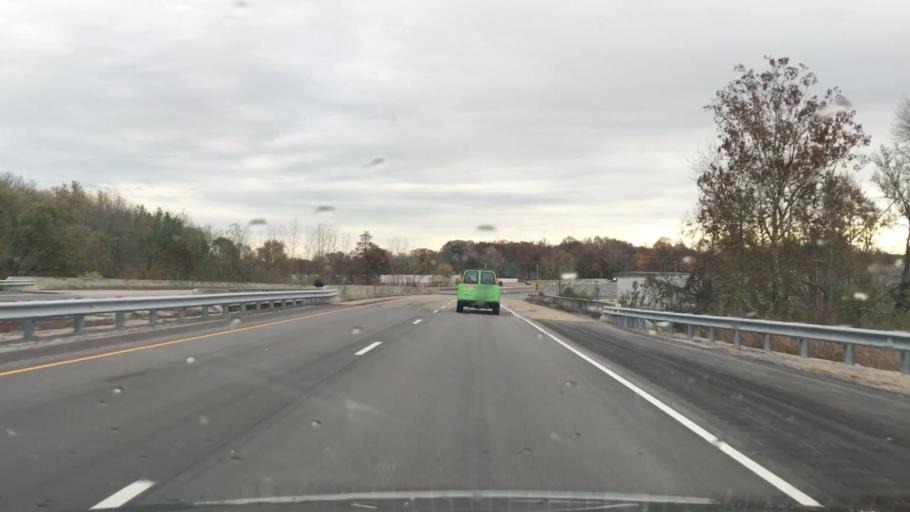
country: US
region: Kentucky
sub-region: Barren County
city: Glasgow
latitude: 37.0341
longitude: -85.9100
